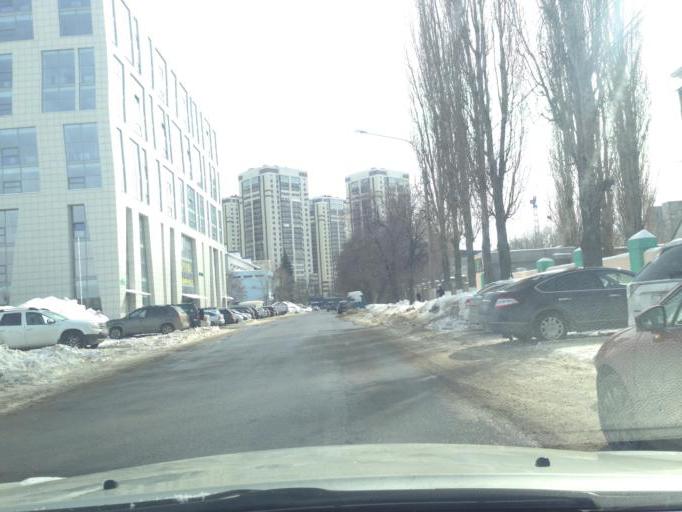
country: RU
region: Voronezj
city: Voronezh
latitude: 51.6576
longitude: 39.1762
